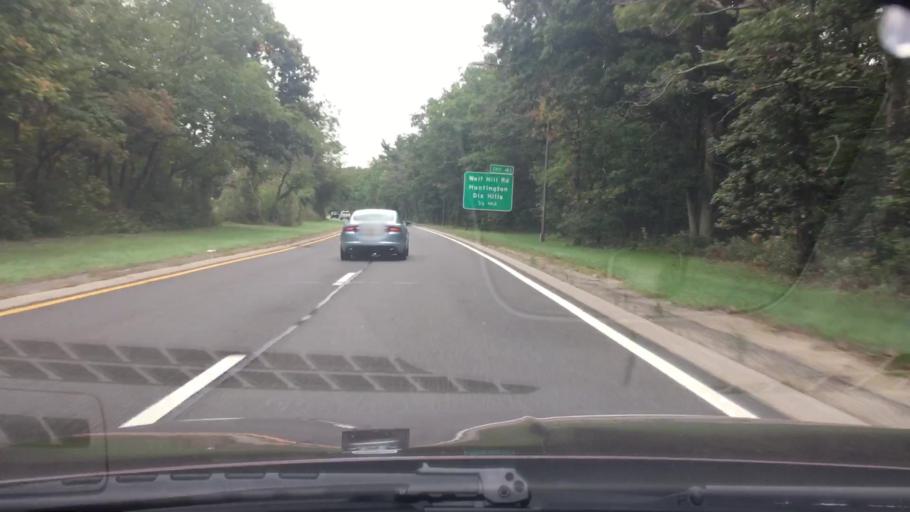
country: US
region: New York
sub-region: Suffolk County
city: South Huntington
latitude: 40.8020
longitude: -73.3869
